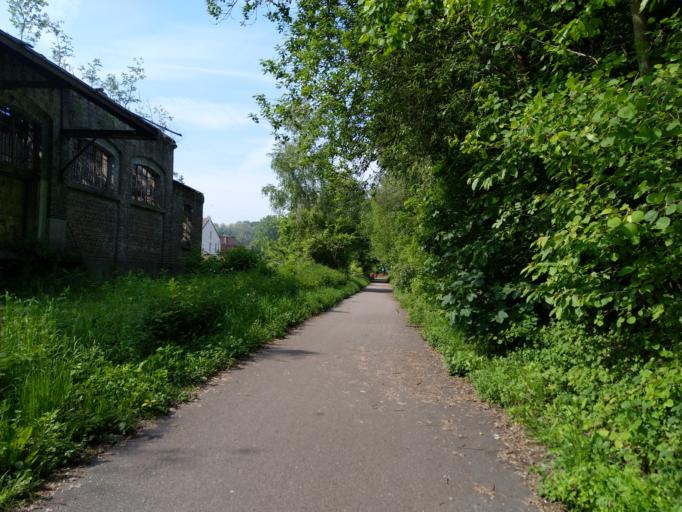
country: BE
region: Wallonia
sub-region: Province du Hainaut
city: Dour
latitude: 50.4044
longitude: 3.7726
